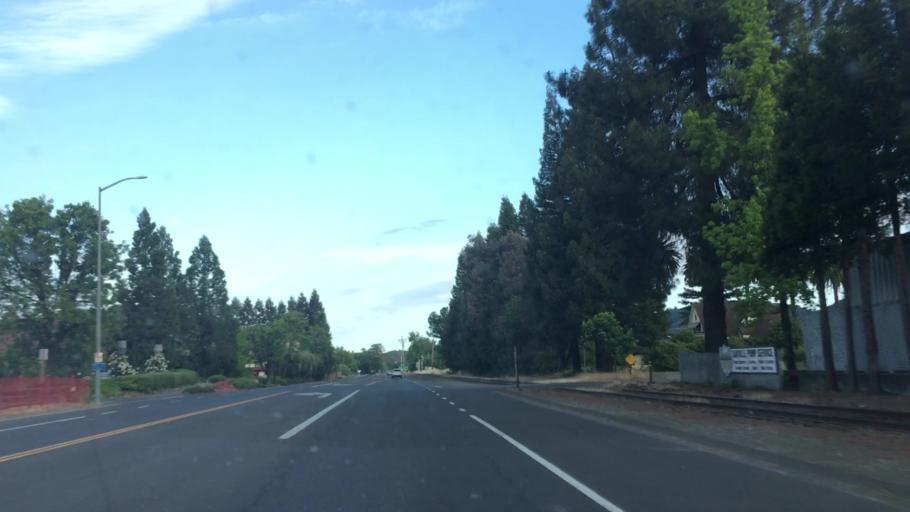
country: US
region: California
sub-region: Napa County
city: Yountville
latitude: 38.4371
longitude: -122.4030
